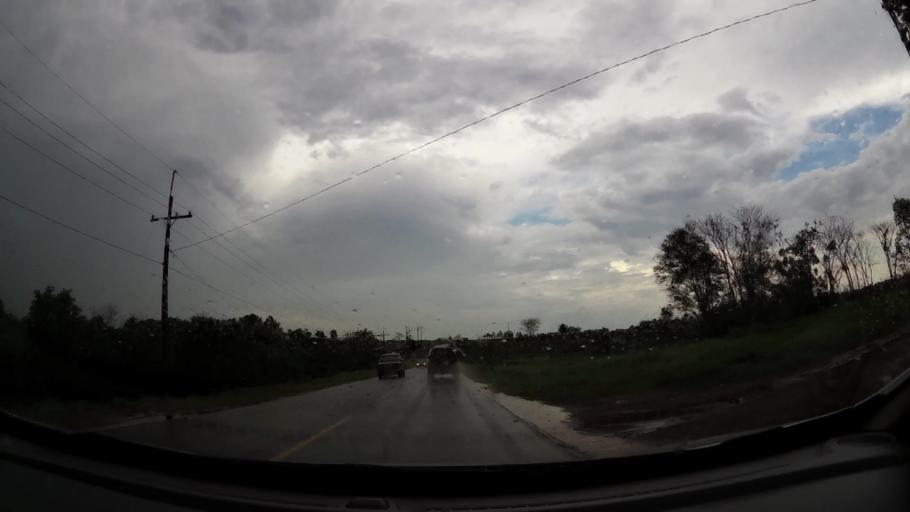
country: PY
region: Alto Parana
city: Presidente Franco
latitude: -25.5815
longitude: -54.6705
